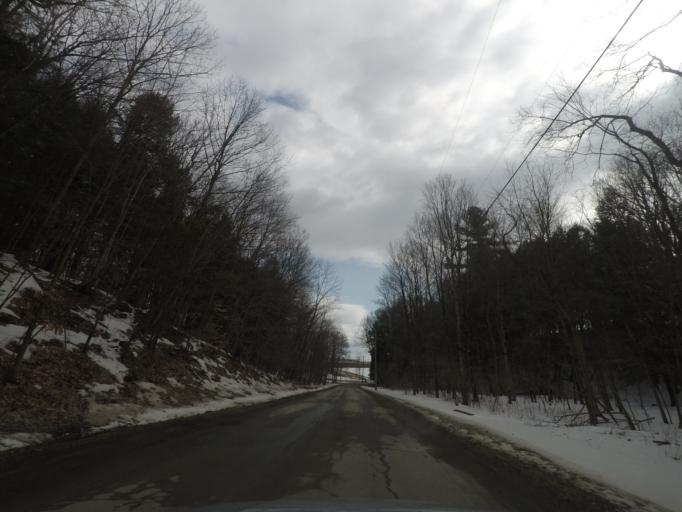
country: US
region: New York
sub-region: Saratoga County
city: Waterford
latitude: 42.7708
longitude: -73.6109
